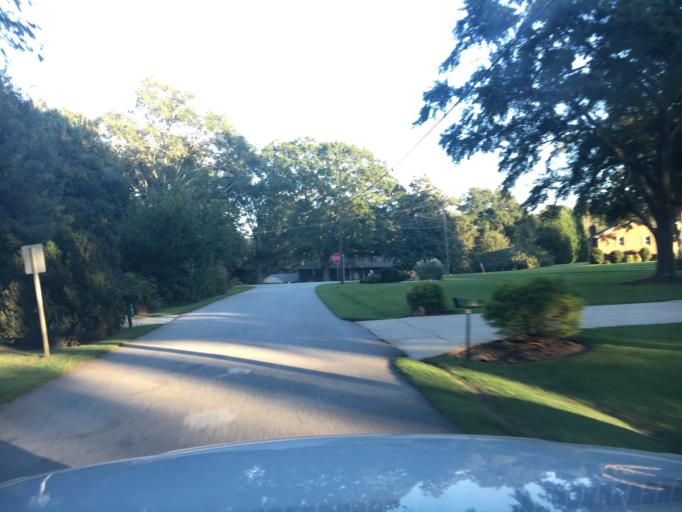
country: US
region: South Carolina
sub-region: Spartanburg County
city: Lyman
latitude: 34.9535
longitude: -82.1211
